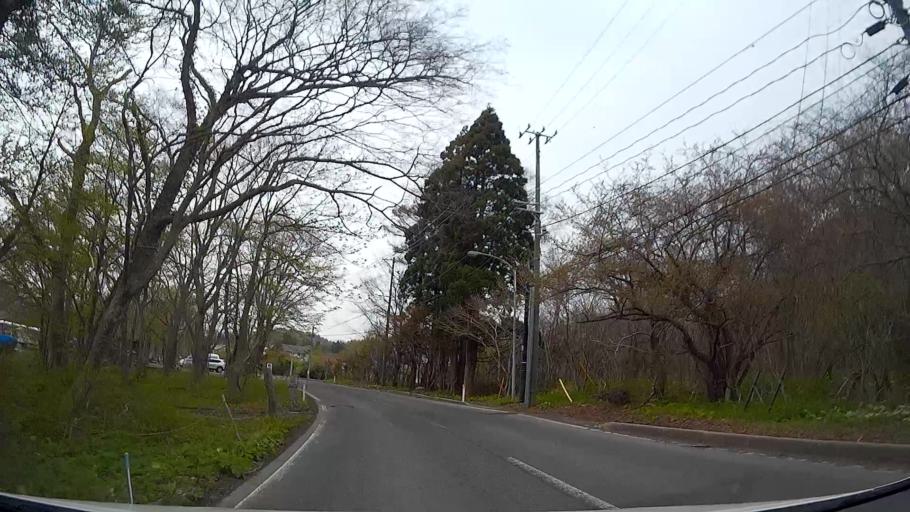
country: JP
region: Akita
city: Hanawa
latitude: 40.4207
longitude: 140.8931
